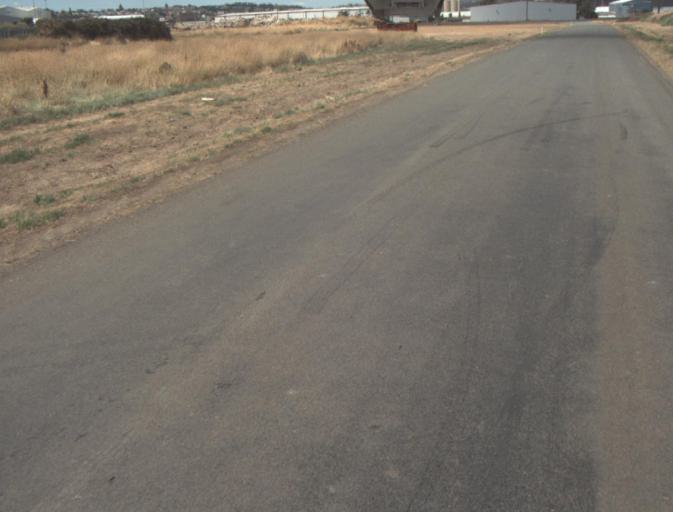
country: AU
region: Tasmania
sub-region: Launceston
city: Launceston
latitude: -41.4212
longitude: 147.1217
